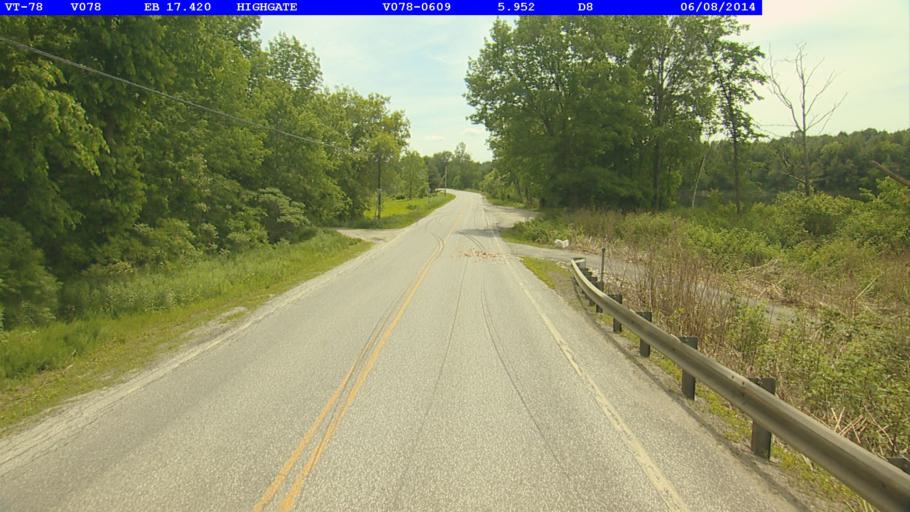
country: US
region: Vermont
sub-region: Franklin County
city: Swanton
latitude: 44.9354
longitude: -72.9953
